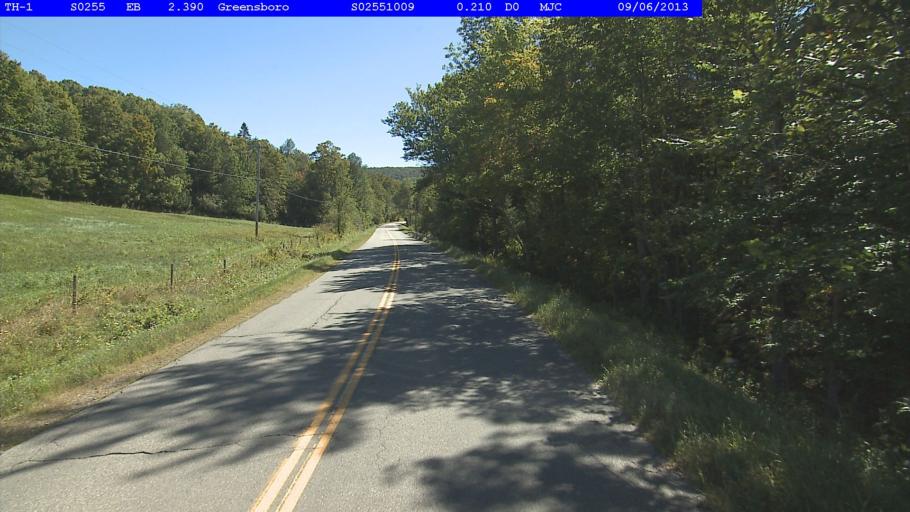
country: US
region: Vermont
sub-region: Caledonia County
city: Hardwick
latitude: 44.6358
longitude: -72.3324
